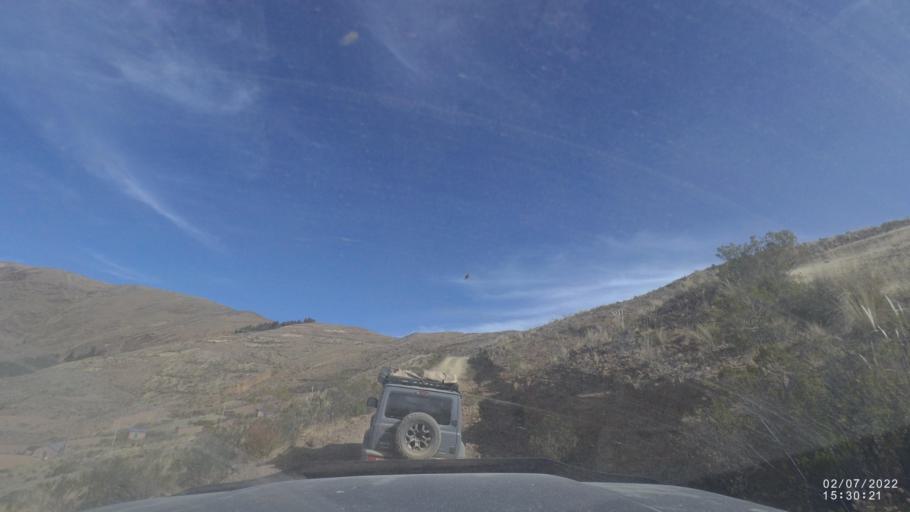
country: BO
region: Cochabamba
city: Irpa Irpa
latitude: -17.8810
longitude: -66.4136
